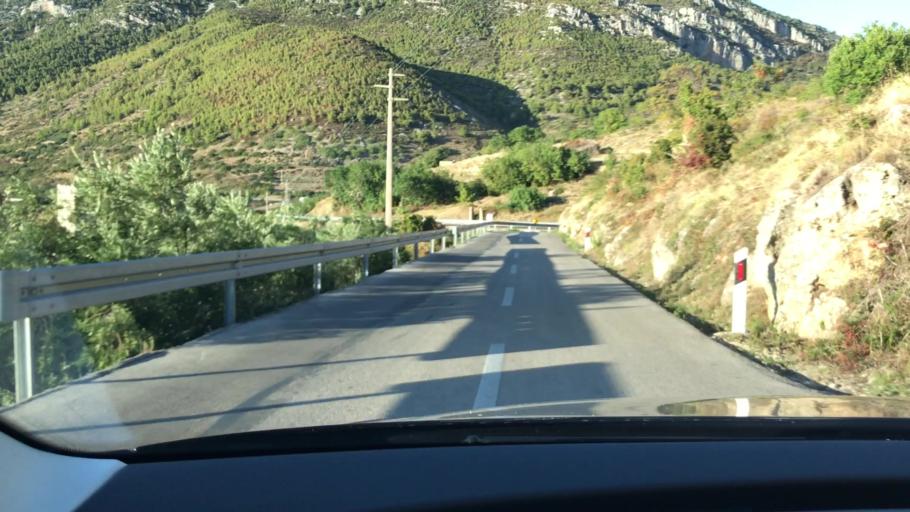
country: HR
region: Splitsko-Dalmatinska
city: Komiza
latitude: 43.0389
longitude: 16.0959
